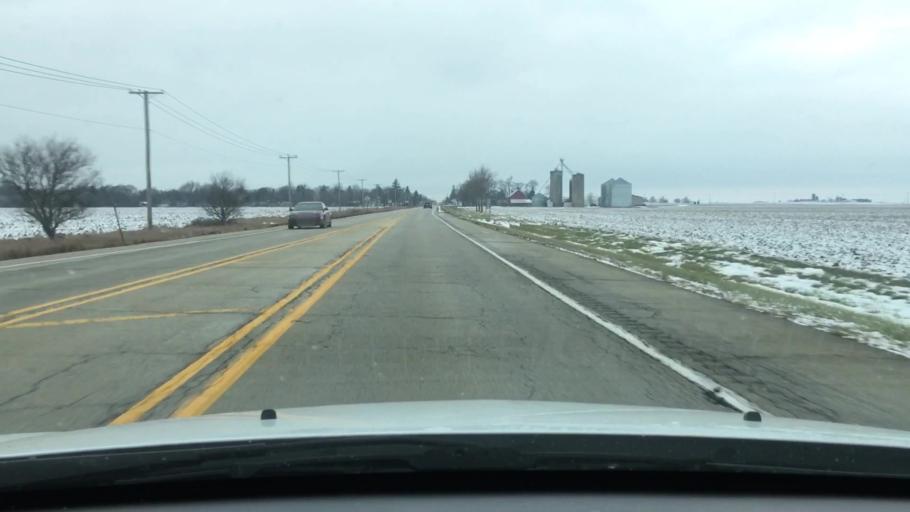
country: US
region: Illinois
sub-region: DeKalb County
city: Malta
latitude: 41.9359
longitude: -88.8487
